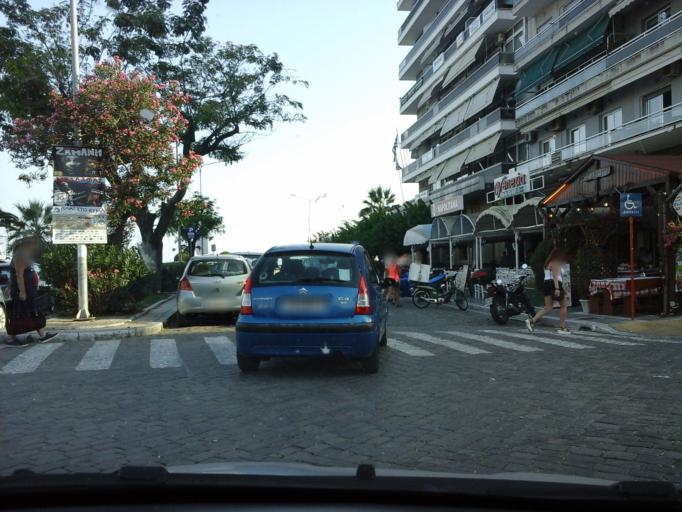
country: GR
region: East Macedonia and Thrace
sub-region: Nomos Kavalas
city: Kavala
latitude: 40.9361
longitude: 24.4093
